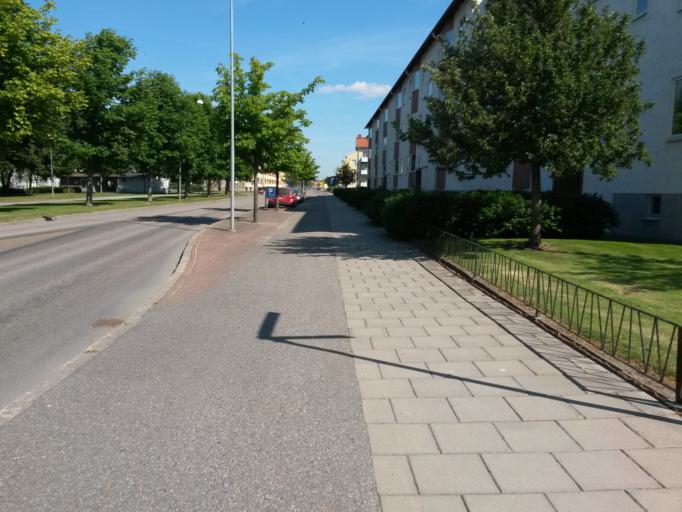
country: SE
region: Vaestra Goetaland
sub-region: Lidkopings Kommun
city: Lidkoping
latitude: 58.4994
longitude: 13.1647
